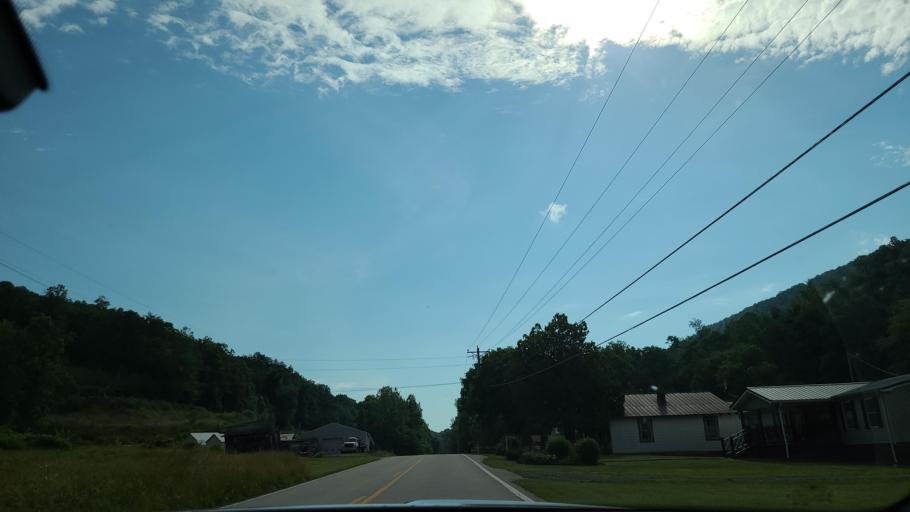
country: US
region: Kentucky
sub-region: Knox County
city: Barbourville
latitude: 36.6804
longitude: -83.9001
